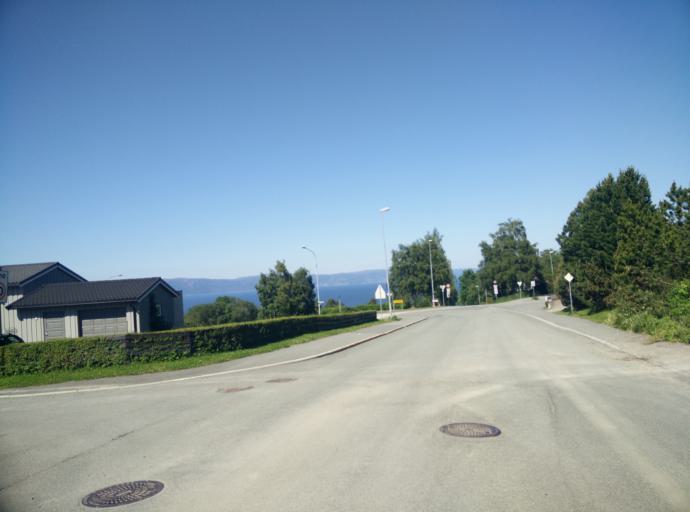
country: NO
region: Sor-Trondelag
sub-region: Trondheim
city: Trondheim
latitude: 63.4228
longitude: 10.3579
